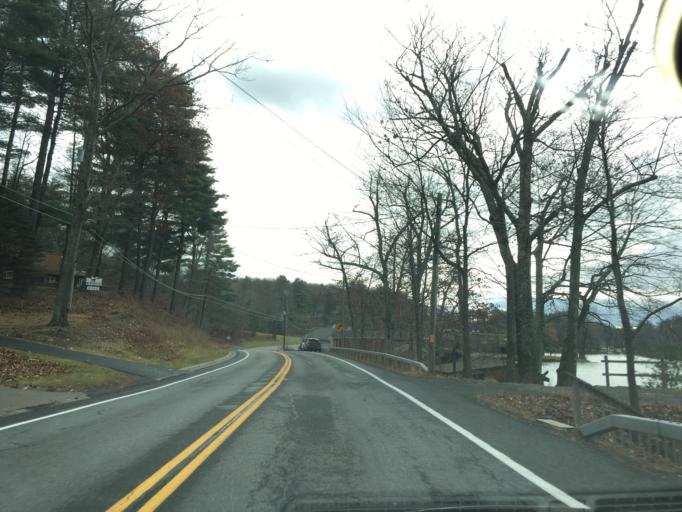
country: US
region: New York
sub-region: Rensselaer County
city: Averill Park
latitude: 42.6104
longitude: -73.5231
